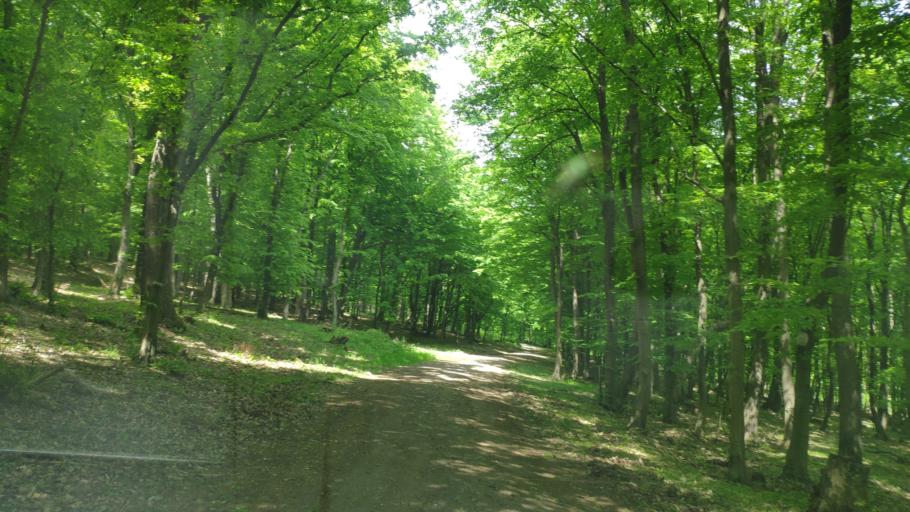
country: SK
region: Kosicky
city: Secovce
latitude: 48.7127
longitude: 21.5809
